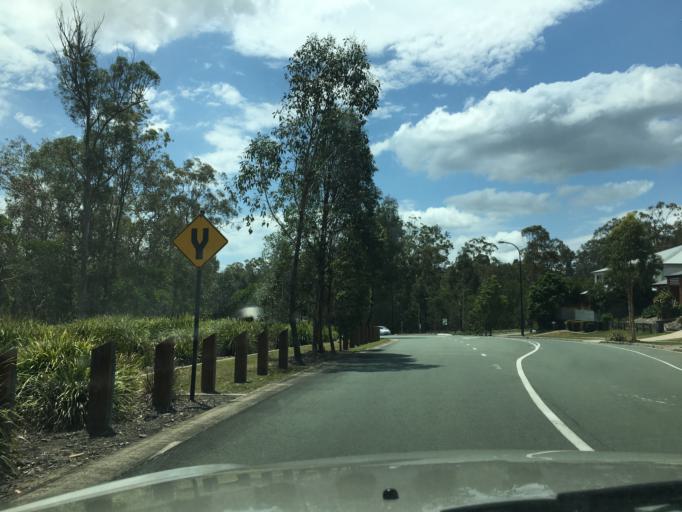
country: AU
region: Queensland
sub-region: Logan
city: Waterford West
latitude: -27.7134
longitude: 153.1492
